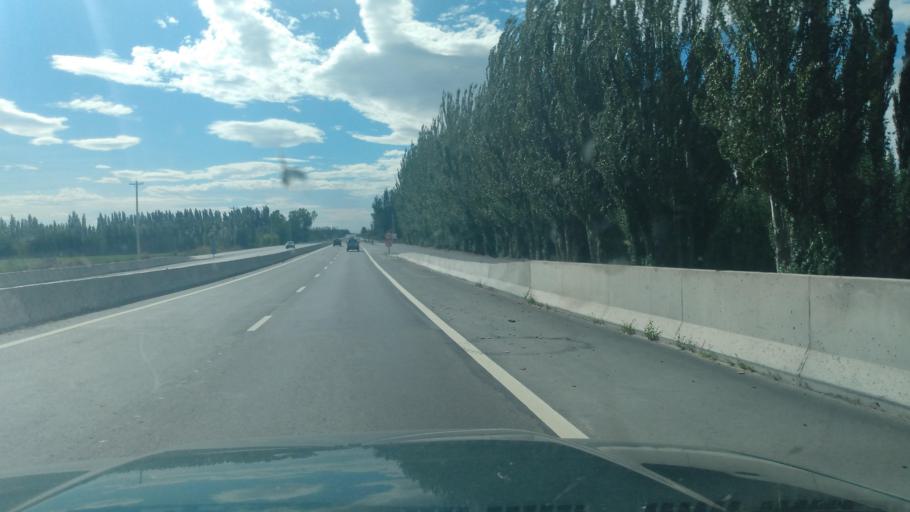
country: AR
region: Rio Negro
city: General Fernandez Oro
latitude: -38.9873
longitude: -67.9197
